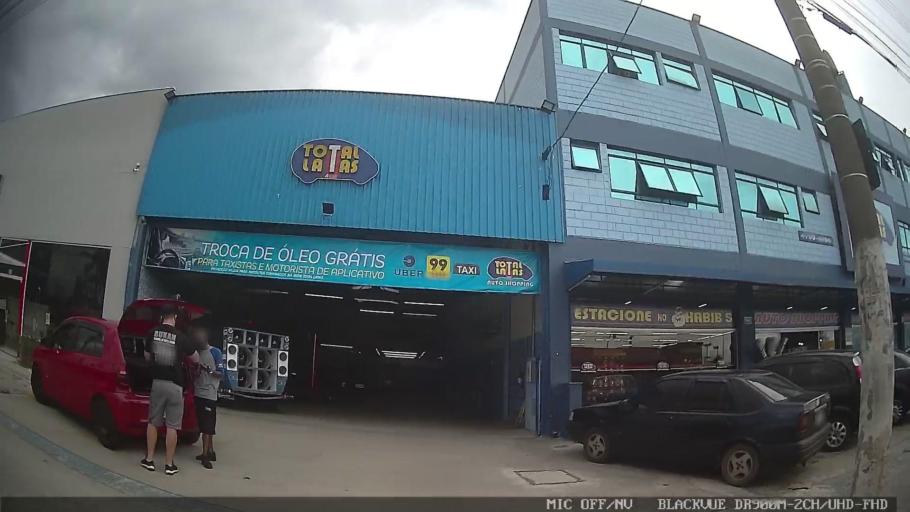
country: BR
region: Sao Paulo
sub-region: Suzano
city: Suzano
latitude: -23.5371
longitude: -46.3011
